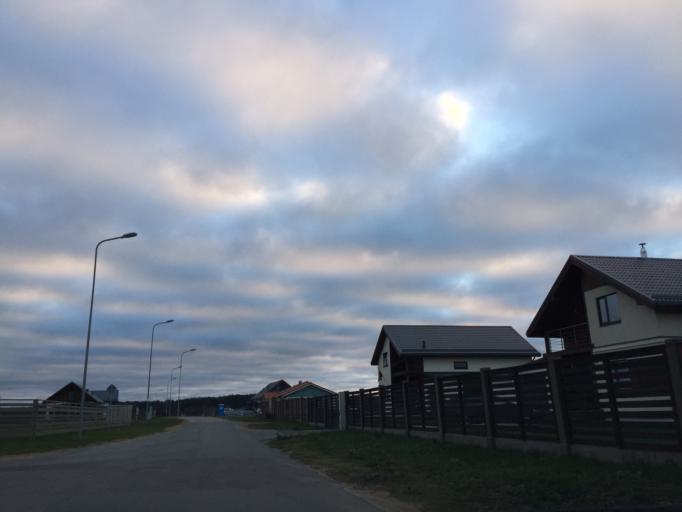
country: LV
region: Adazi
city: Adazi
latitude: 57.0681
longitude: 24.3459
